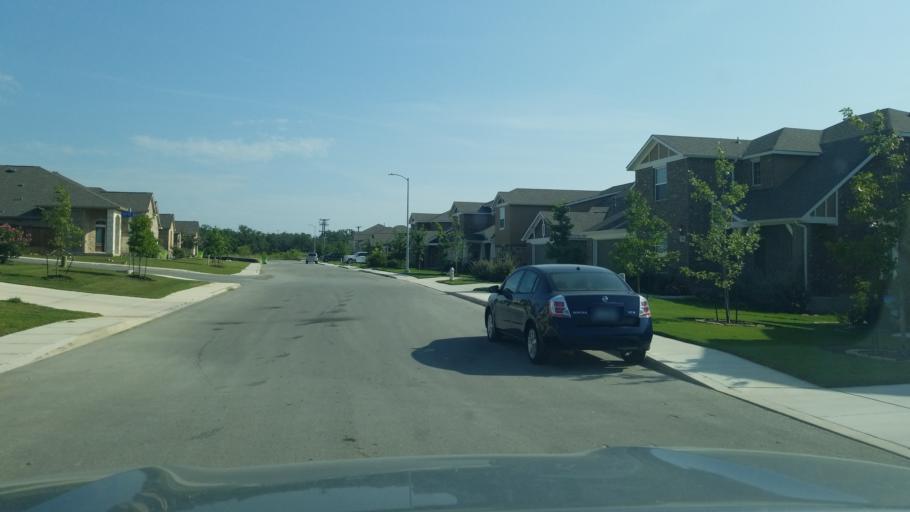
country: US
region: Texas
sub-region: Medina County
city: La Coste
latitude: 29.4024
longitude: -98.7800
